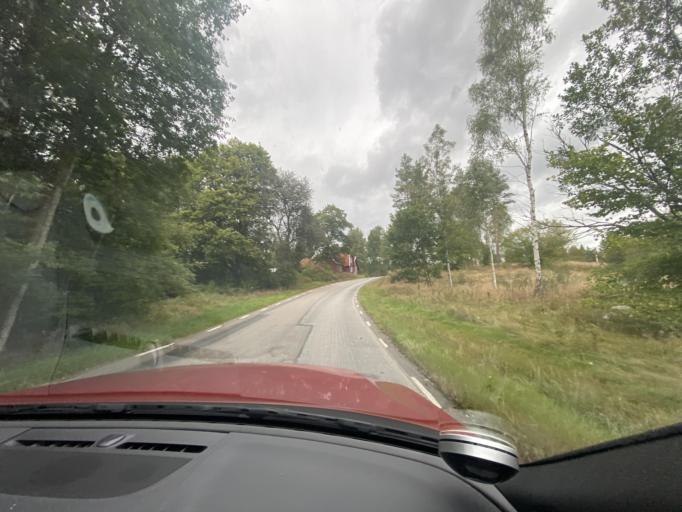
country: SE
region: Kronoberg
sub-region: Markaryds Kommun
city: Markaryd
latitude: 56.4871
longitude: 13.5910
